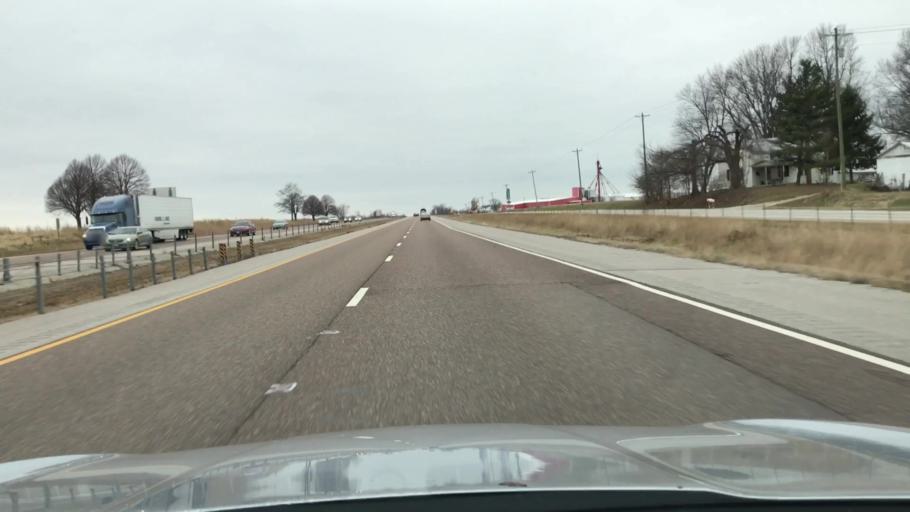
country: US
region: Illinois
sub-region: Madison County
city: Worden
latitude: 38.9284
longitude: -89.8049
